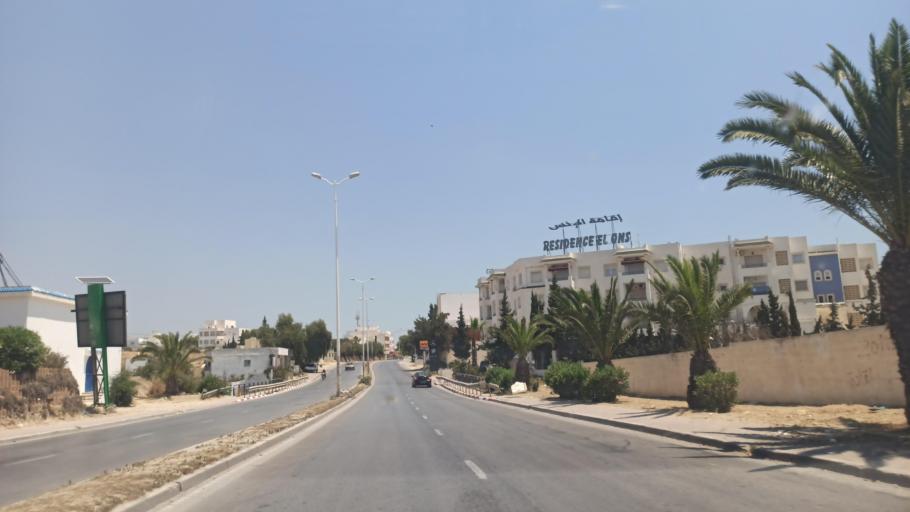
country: TN
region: Nabul
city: Al Hammamat
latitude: 36.4089
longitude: 10.6402
